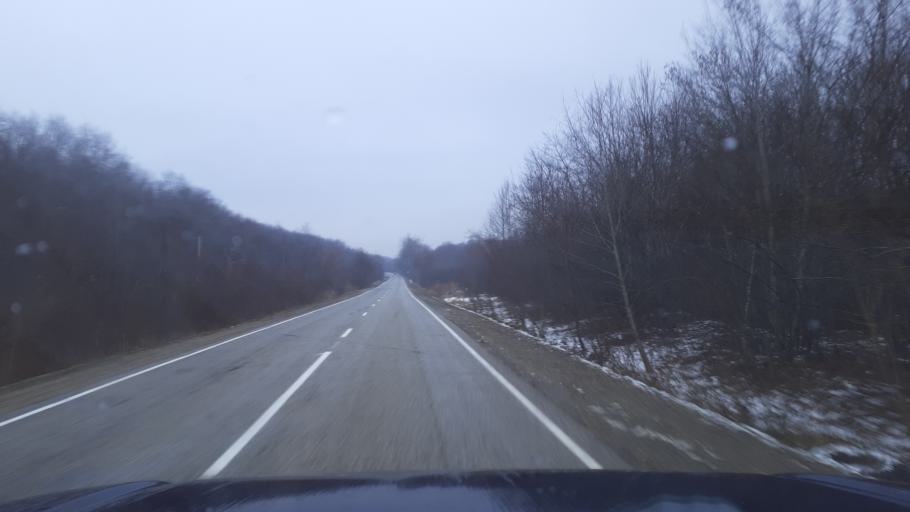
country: RU
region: Krasnodarskiy
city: Neftegorsk
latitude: 44.2784
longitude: 39.7943
